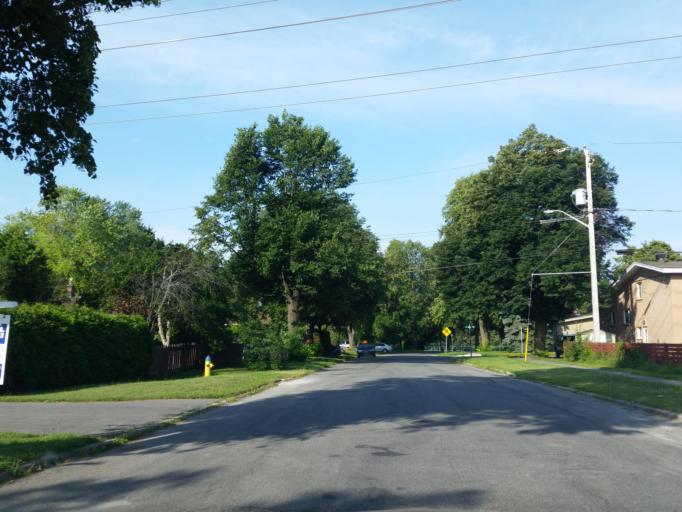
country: CA
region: Ontario
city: Ottawa
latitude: 45.3592
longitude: -75.7472
